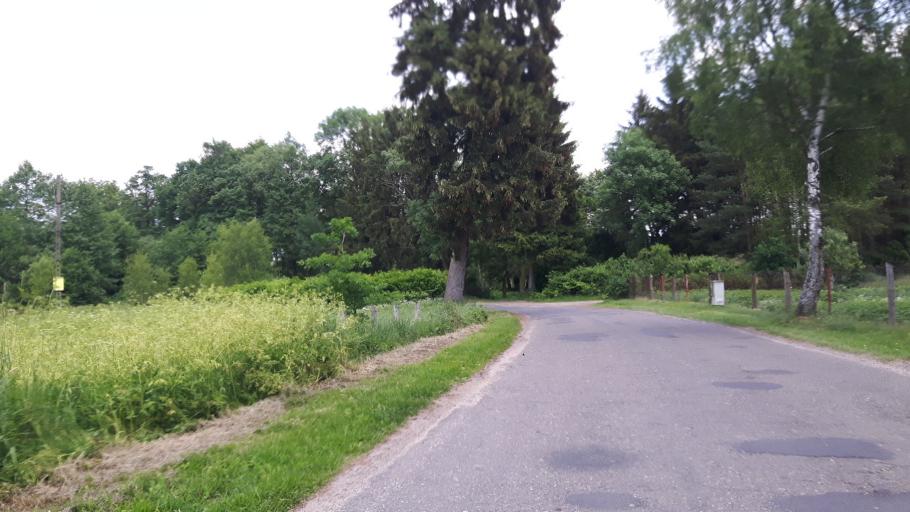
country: PL
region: West Pomeranian Voivodeship
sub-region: Powiat goleniowski
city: Osina
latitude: 53.6427
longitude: 14.9356
